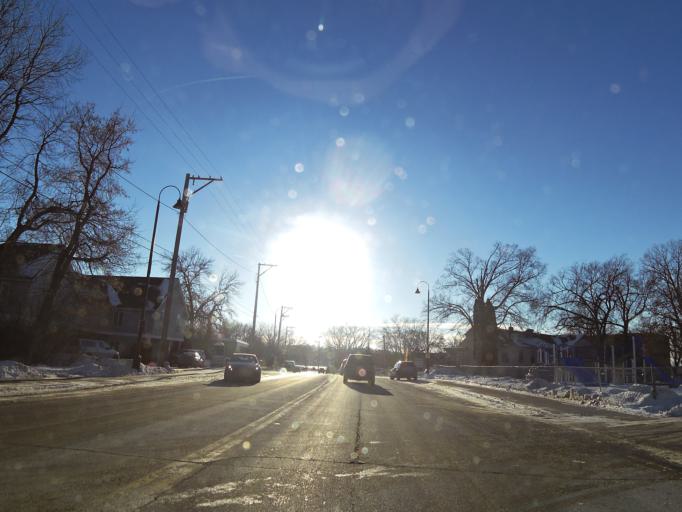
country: US
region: Minnesota
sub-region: Hennepin County
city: Mound
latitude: 44.9344
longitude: -93.6671
